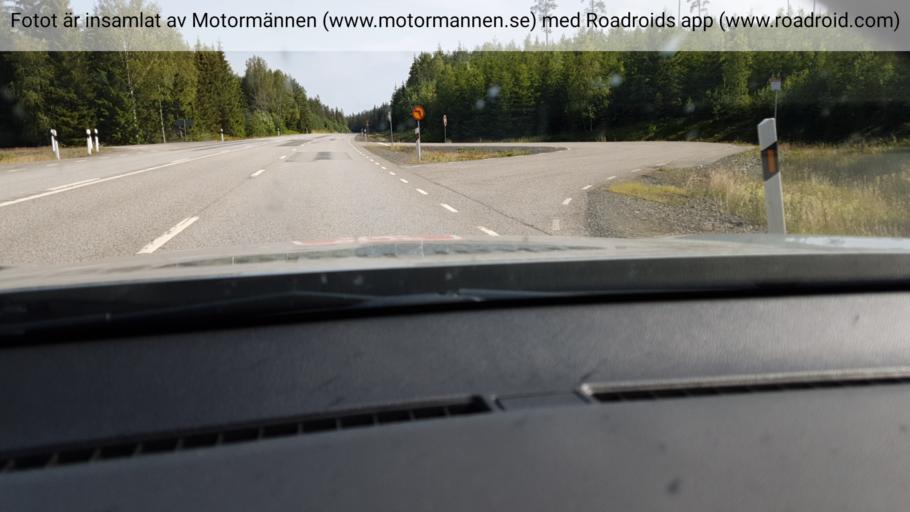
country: SE
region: Joenkoeping
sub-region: Aneby Kommun
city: Aneby
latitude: 57.7816
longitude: 14.8841
